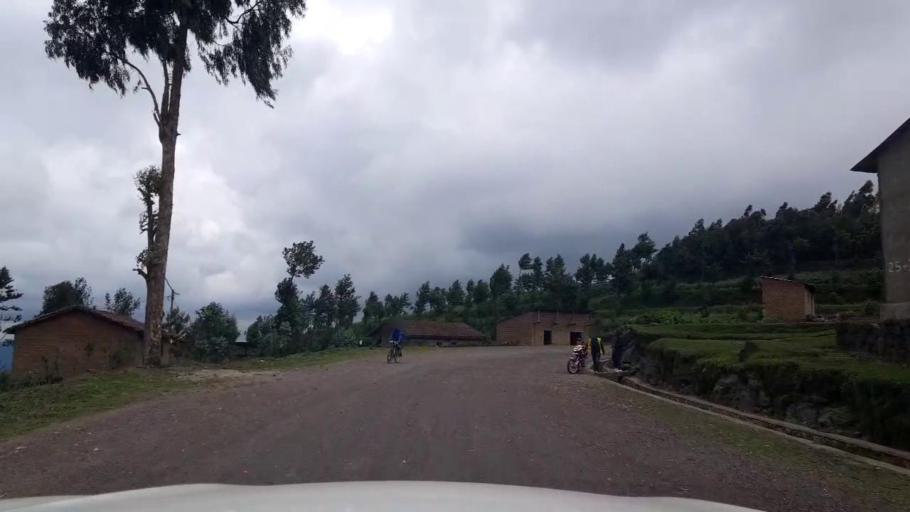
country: RW
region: Northern Province
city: Musanze
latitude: -1.5806
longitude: 29.4812
